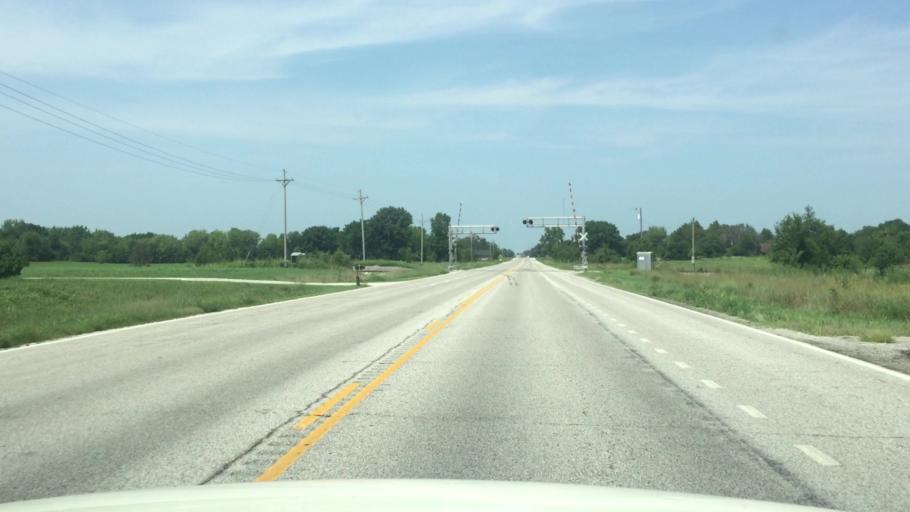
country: US
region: Kansas
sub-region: Cherokee County
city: Galena
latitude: 37.1125
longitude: -94.7044
